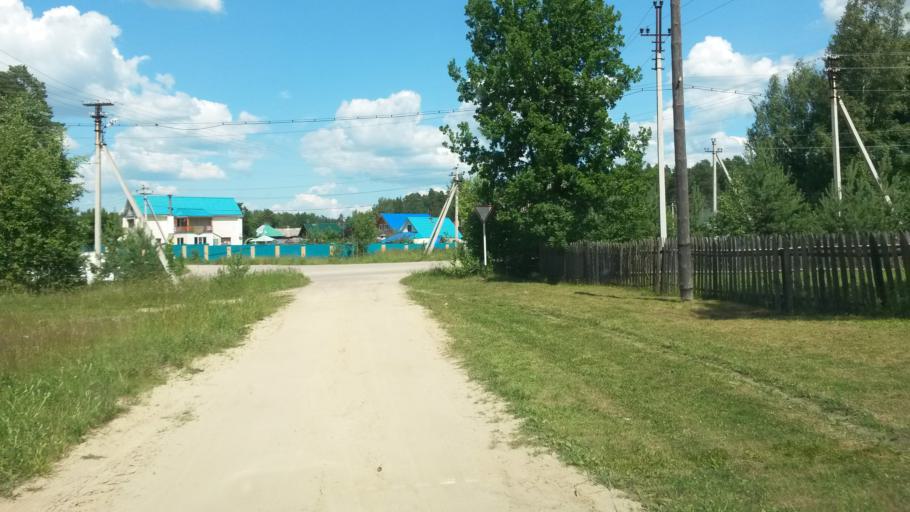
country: RU
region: Ivanovo
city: Zarechnyy
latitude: 57.4996
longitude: 42.3316
